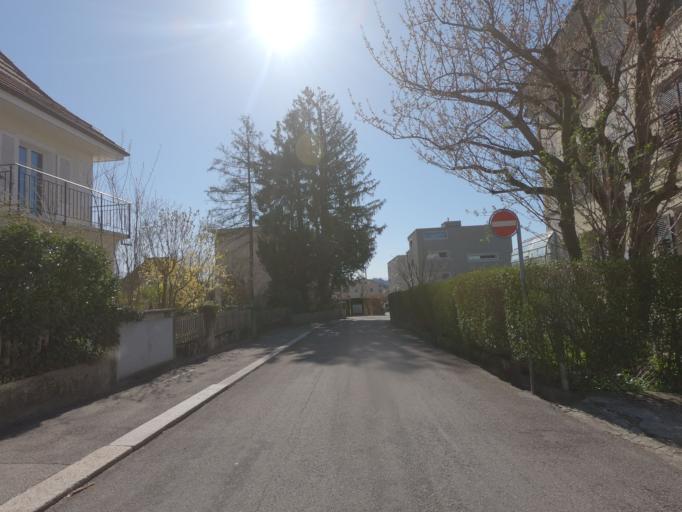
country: CH
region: Solothurn
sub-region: Bezirk Solothurn
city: Solothurn
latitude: 47.2144
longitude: 7.5461
